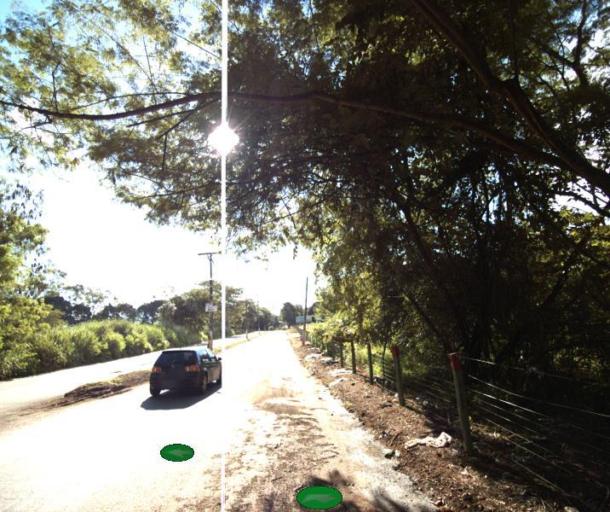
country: BR
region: Goias
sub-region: Rialma
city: Rialma
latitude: -15.3323
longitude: -49.5714
